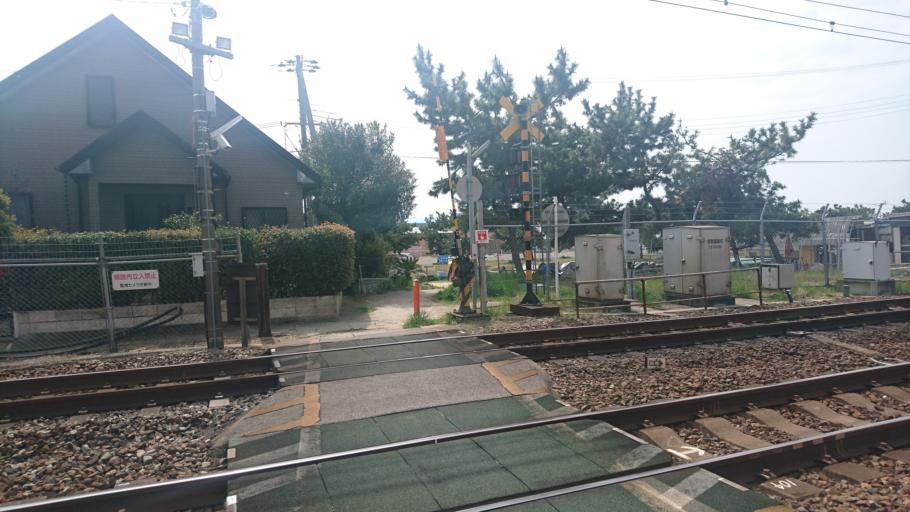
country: JP
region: Hyogo
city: Kobe
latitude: 34.6417
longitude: 135.1097
